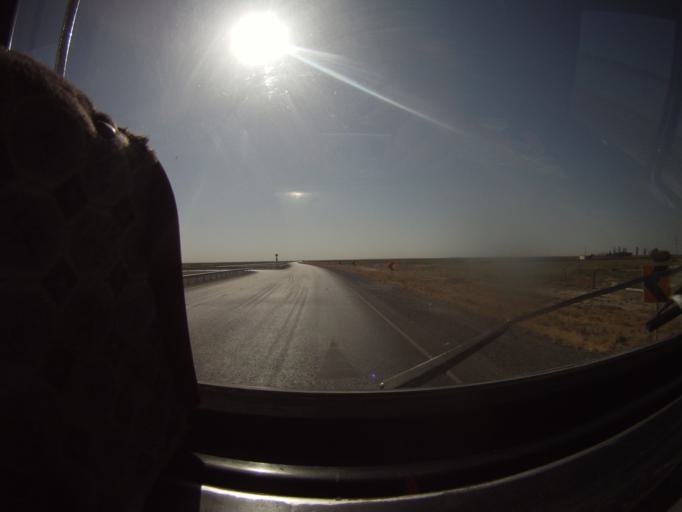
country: KZ
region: Qyzylorda
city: Zhangaqorghan
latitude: 43.9994
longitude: 67.2196
